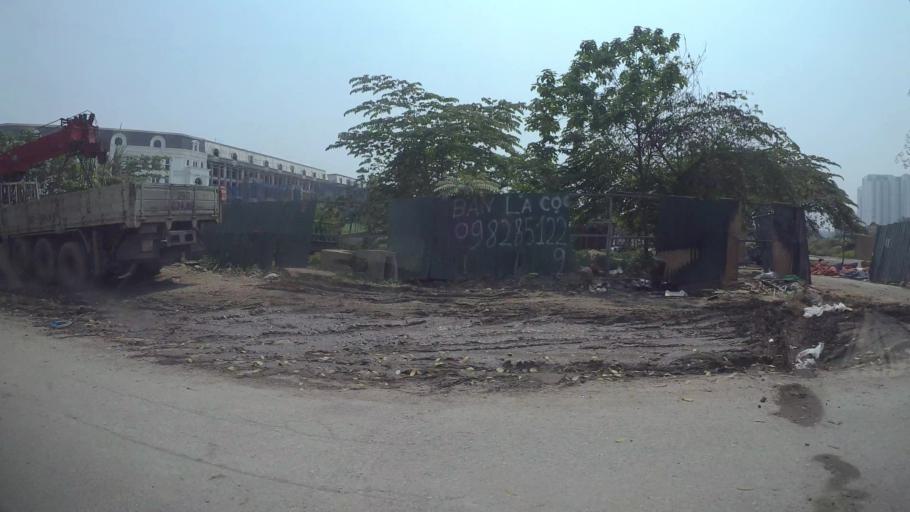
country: VN
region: Ha Noi
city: Ha Dong
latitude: 20.9898
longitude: 105.7643
